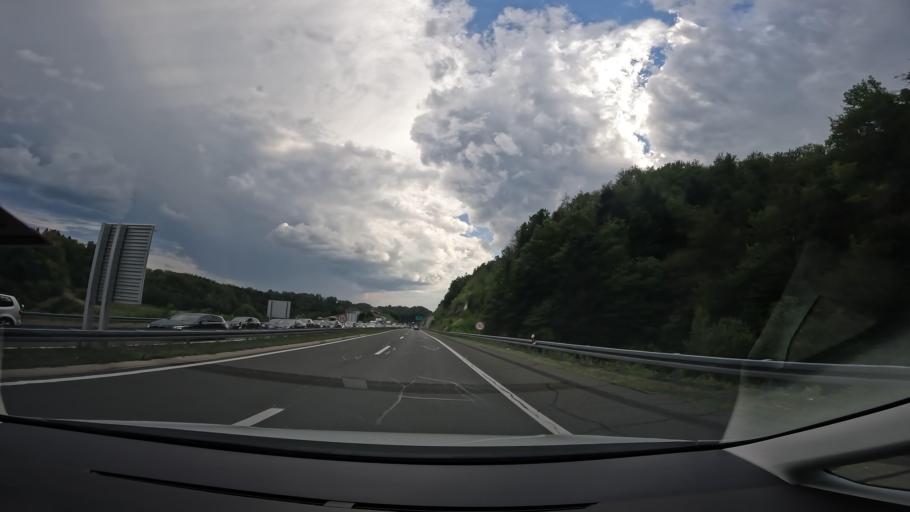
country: SI
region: Zetale
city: Zetale
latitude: 46.2582
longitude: 15.8572
